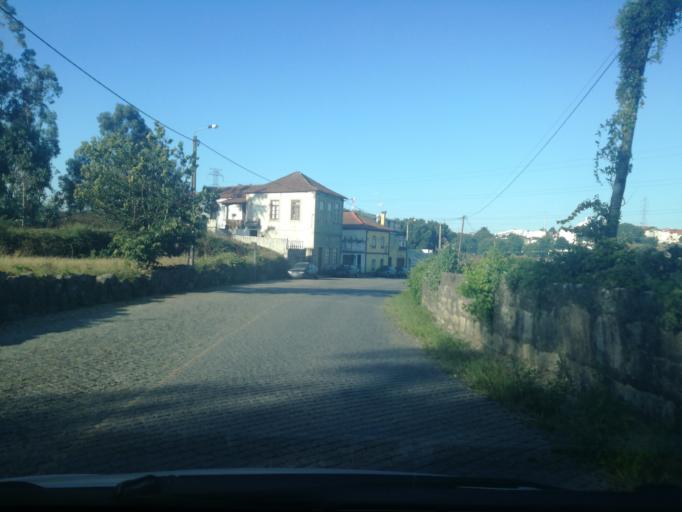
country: PT
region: Porto
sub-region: Maia
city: Leca do Bailio
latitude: 41.2086
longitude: -8.6178
